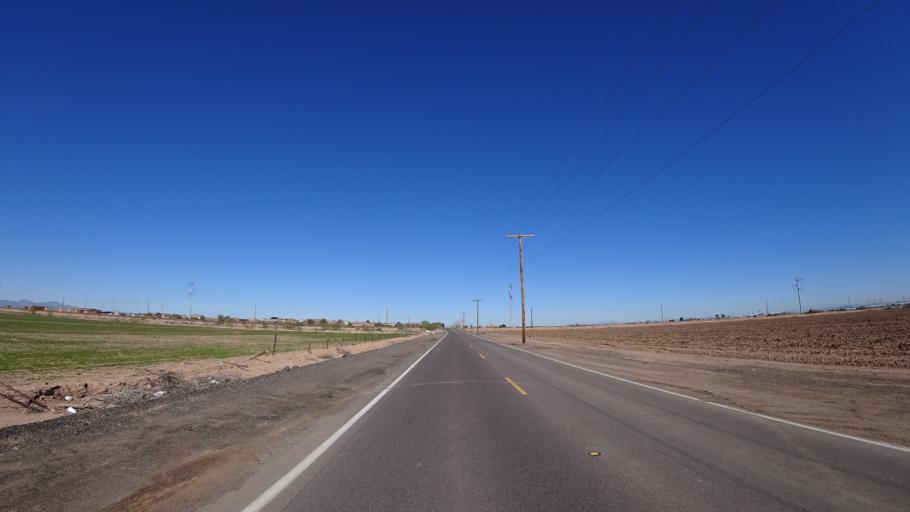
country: US
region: Arizona
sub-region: Maricopa County
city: Tolleson
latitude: 33.3967
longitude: -112.2722
